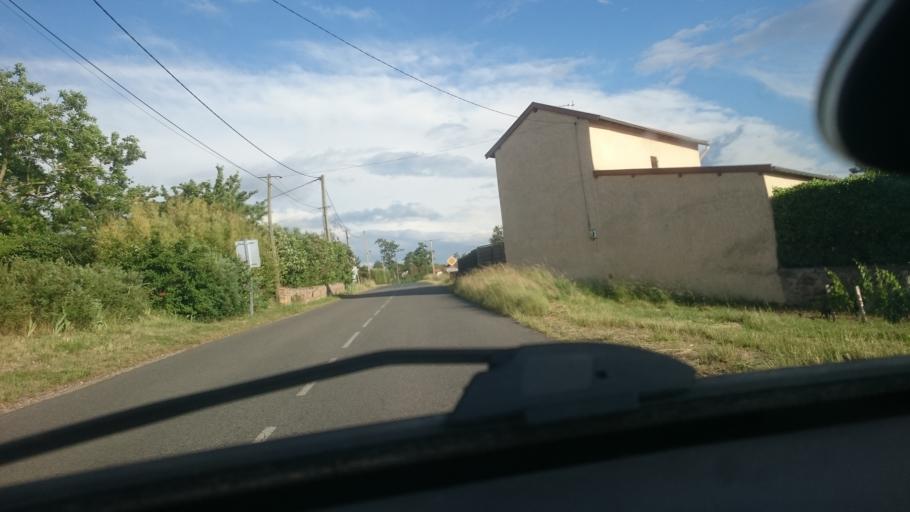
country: FR
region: Rhone-Alpes
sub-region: Departement du Rhone
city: Bully
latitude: 45.8812
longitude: 4.5620
